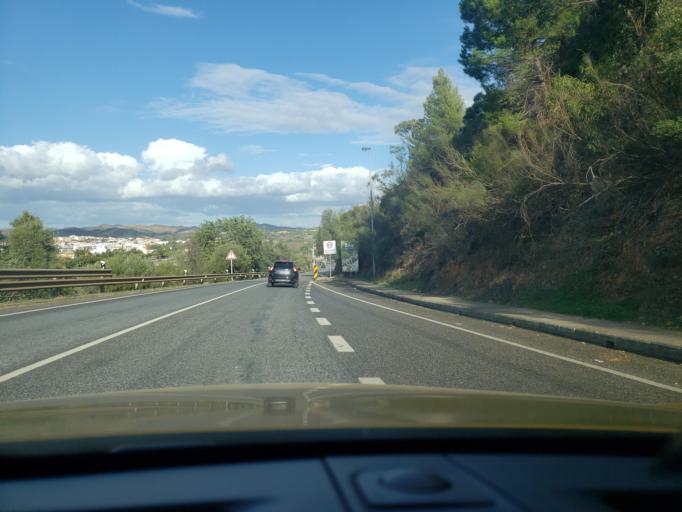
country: PT
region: Faro
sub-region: Silves
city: Silves
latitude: 37.1839
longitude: -8.4387
